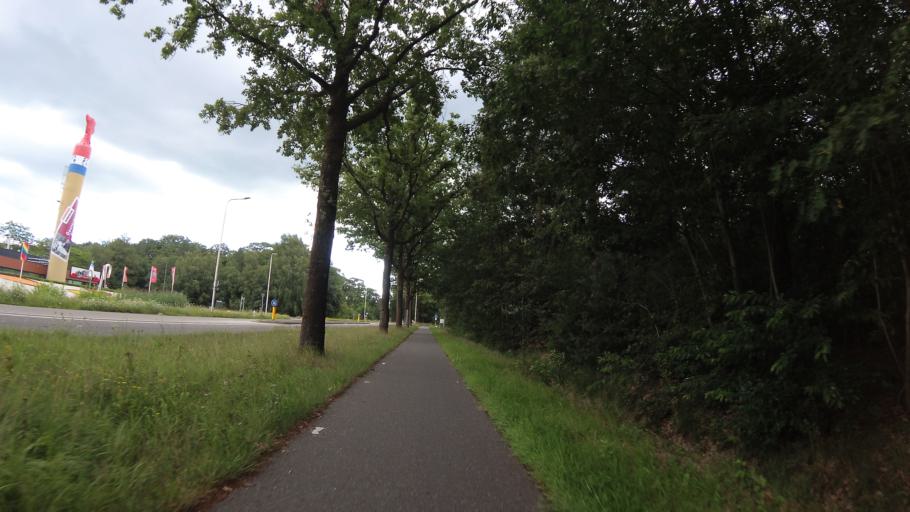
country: NL
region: North Brabant
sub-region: Gemeente Oosterhout
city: Oosterhout
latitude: 51.6188
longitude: 4.8800
